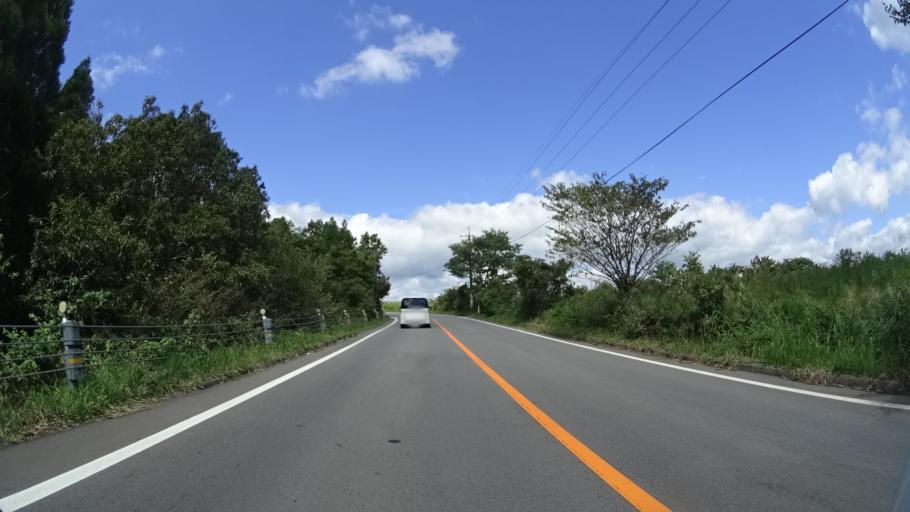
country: JP
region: Kumamoto
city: Aso
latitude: 33.0078
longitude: 131.1172
